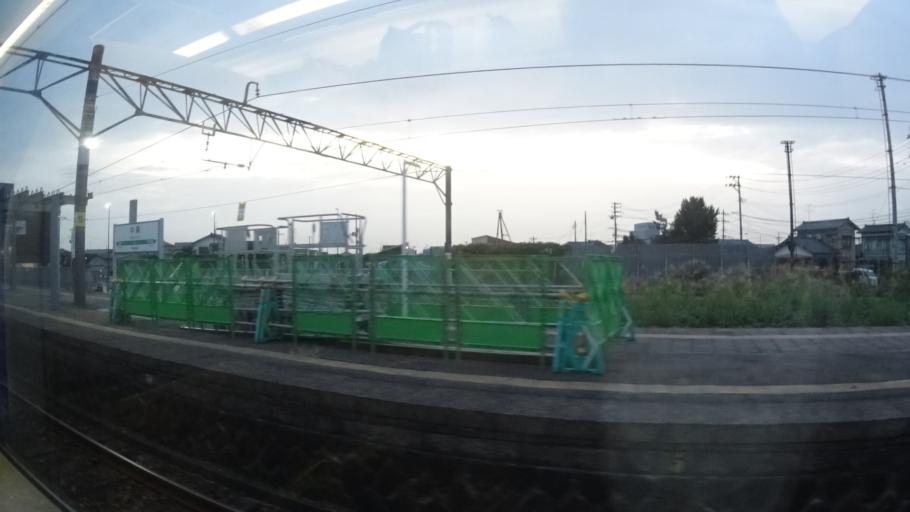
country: JP
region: Niigata
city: Shibata
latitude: 38.0508
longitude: 139.3986
